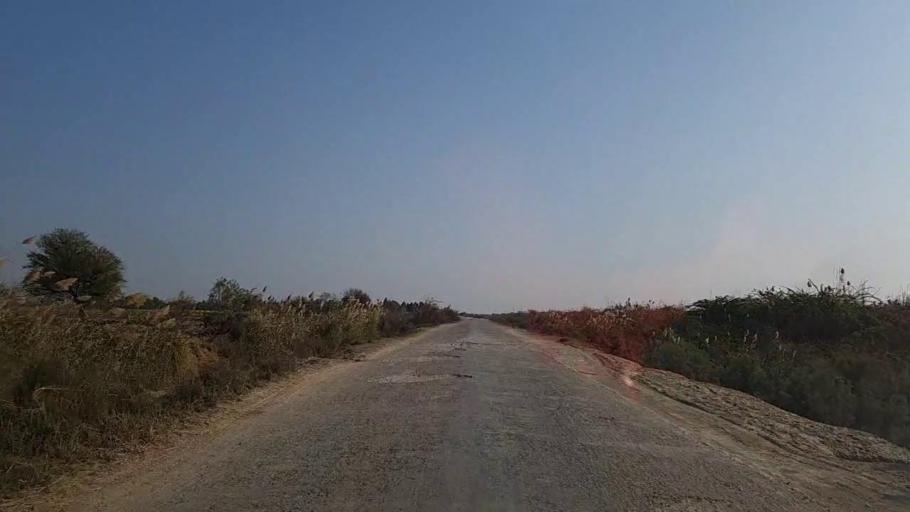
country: PK
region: Sindh
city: Tando Mittha Khan
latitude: 25.9212
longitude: 69.0700
